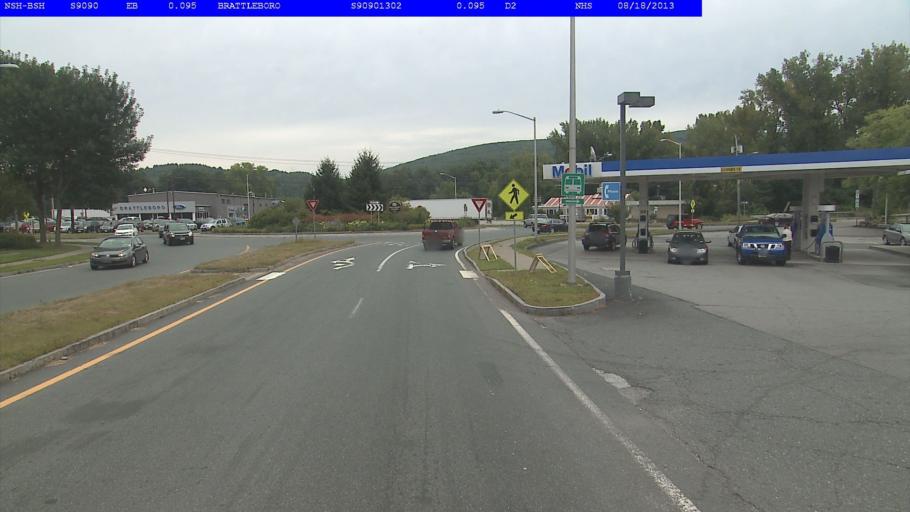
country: US
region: Vermont
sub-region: Windham County
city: Brattleboro
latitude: 42.8852
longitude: -72.5575
